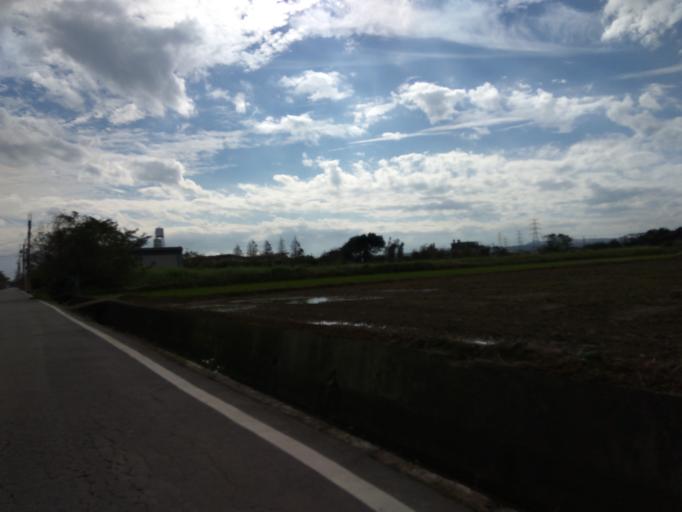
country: TW
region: Taiwan
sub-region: Hsinchu
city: Zhubei
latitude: 24.9534
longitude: 121.1070
